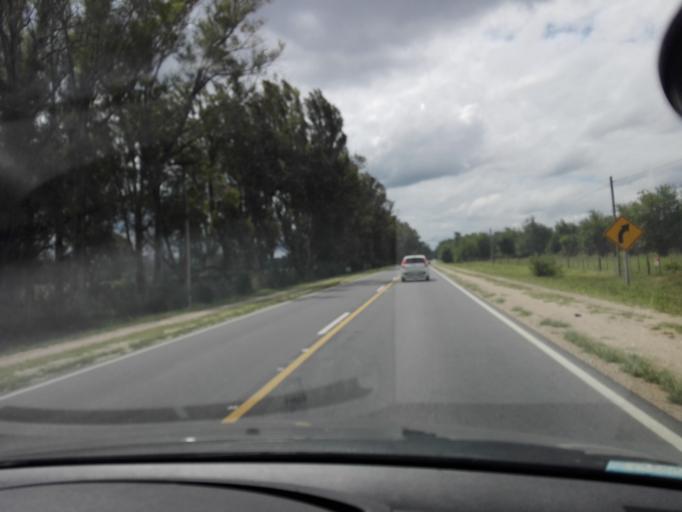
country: AR
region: Cordoba
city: Alta Gracia
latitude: -31.6041
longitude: -64.4486
